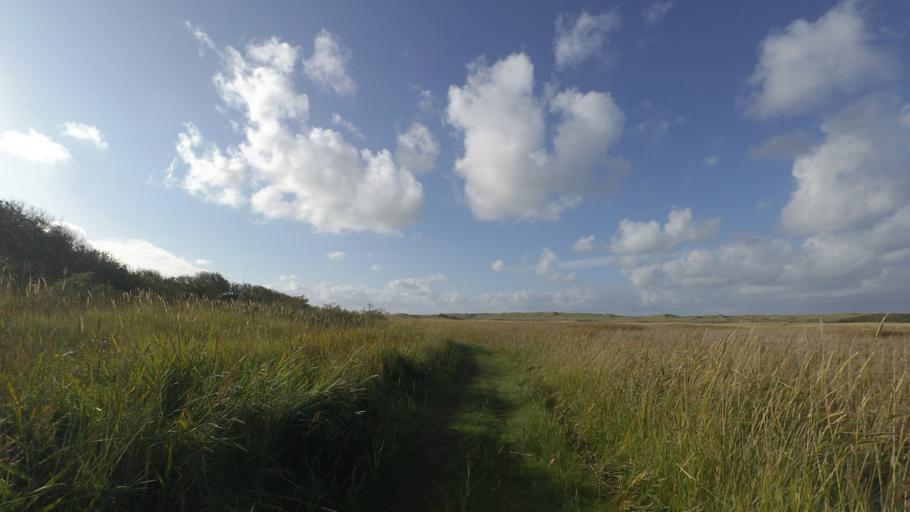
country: NL
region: Friesland
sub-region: Gemeente Dongeradeel
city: Ternaard
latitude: 53.4611
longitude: 5.9190
